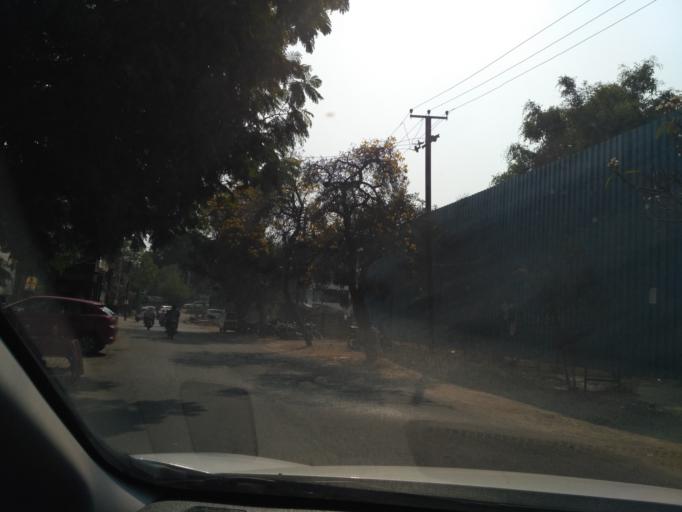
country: IN
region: Telangana
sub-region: Rangareddi
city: Kukatpalli
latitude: 17.4364
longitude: 78.4007
